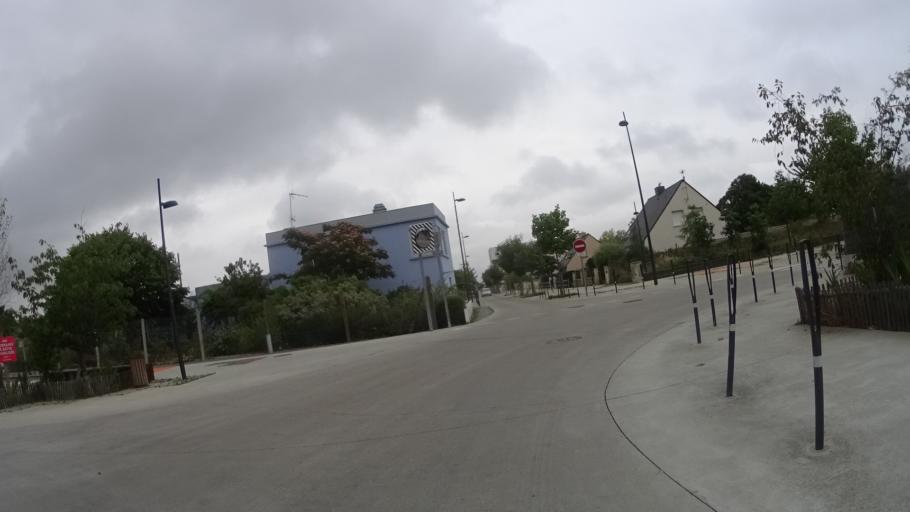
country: FR
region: Pays de la Loire
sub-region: Departement de la Loire-Atlantique
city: Saint-Nazaire
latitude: 47.2996
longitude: -2.2013
